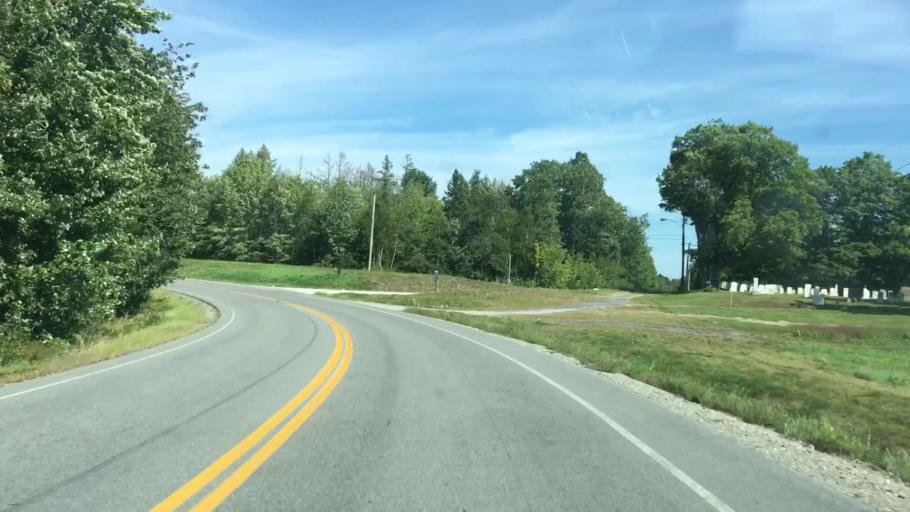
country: US
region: Maine
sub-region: Penobscot County
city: Bradford
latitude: 45.1677
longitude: -68.8416
